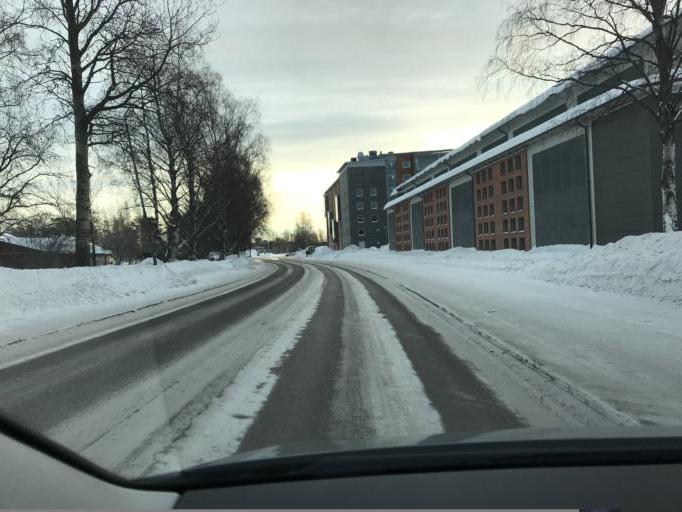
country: SE
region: Norrbotten
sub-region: Lulea Kommun
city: Bergnaset
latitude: 65.6023
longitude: 22.1260
